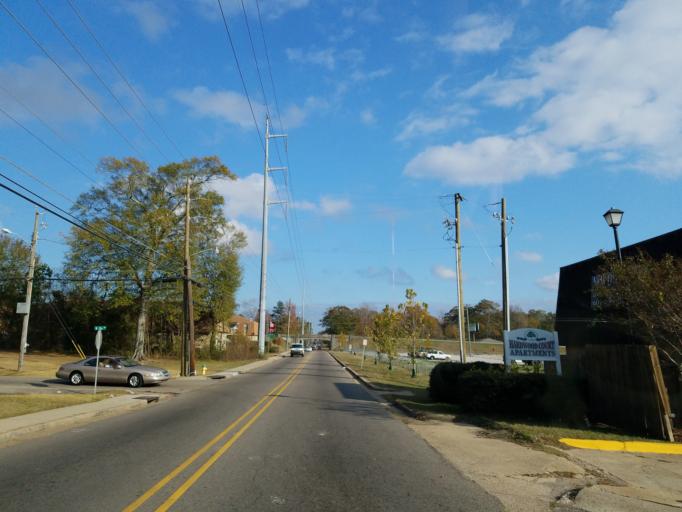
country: US
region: Mississippi
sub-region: Forrest County
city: Glendale
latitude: 31.3357
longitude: -89.3316
